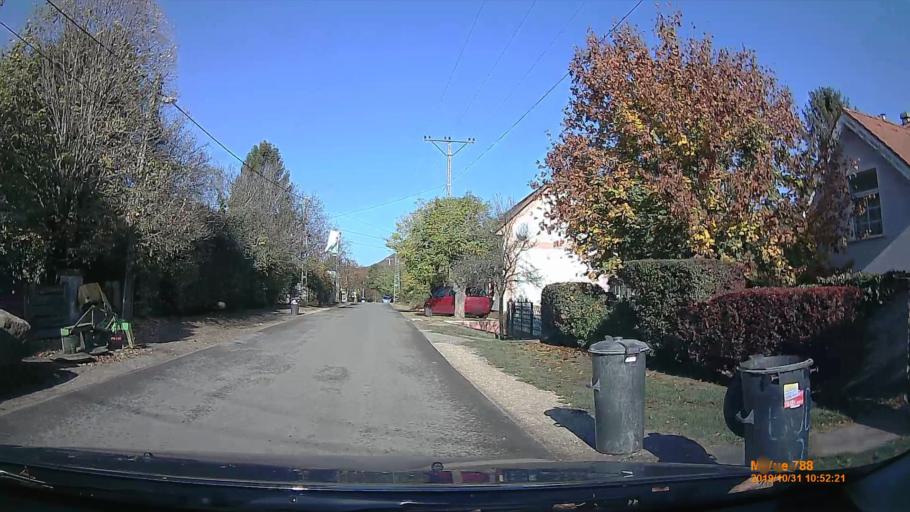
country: HU
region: Pest
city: Pilisborosjeno
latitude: 47.6025
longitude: 18.9934
